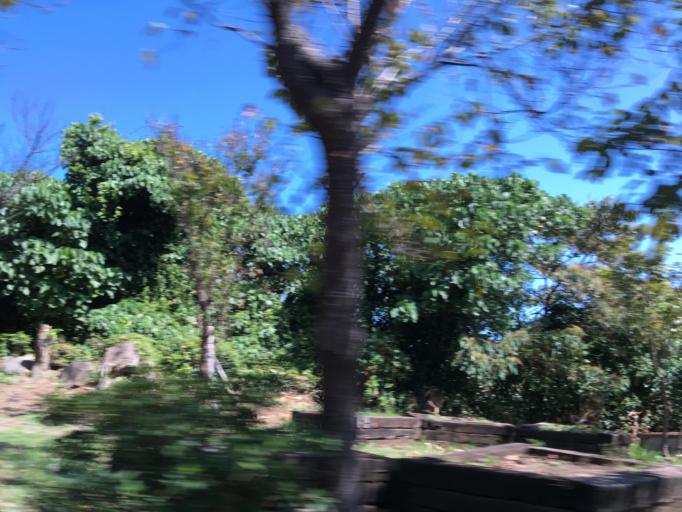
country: TW
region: Taipei
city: Taipei
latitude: 25.1498
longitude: 121.5045
